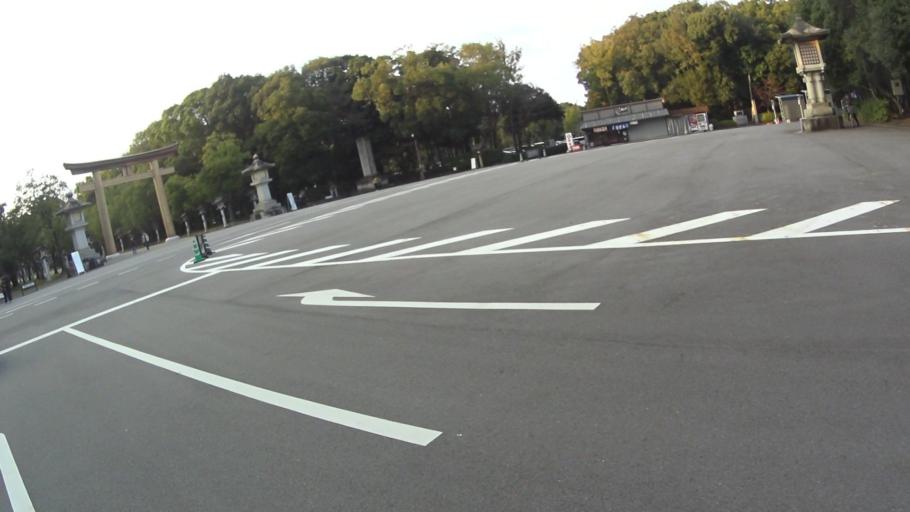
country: JP
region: Nara
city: Kashihara-shi
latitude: 34.4863
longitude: 135.7904
